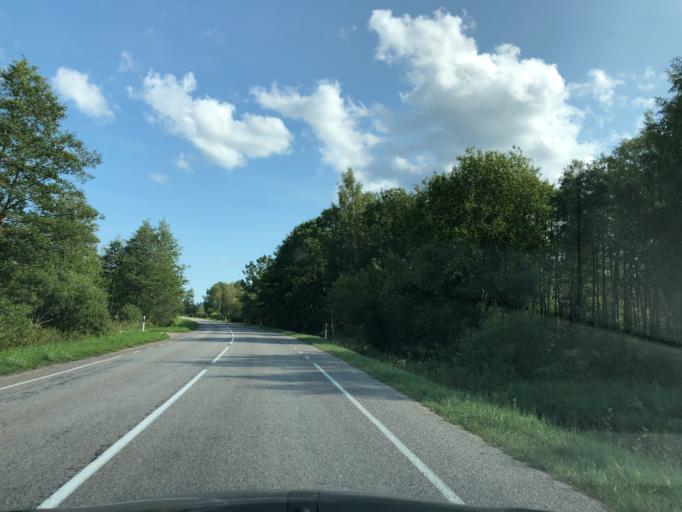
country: EE
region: Hiiumaa
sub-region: Kaerdla linn
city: Kardla
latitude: 58.7190
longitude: 22.5648
